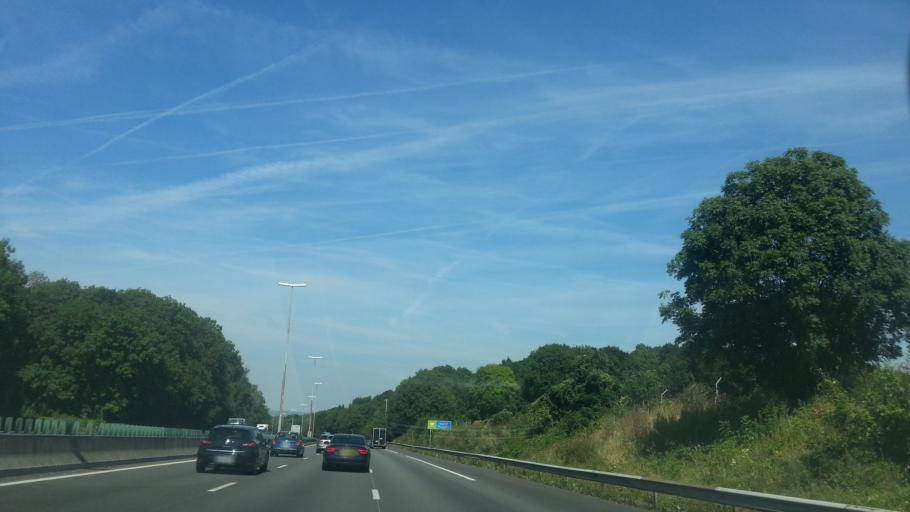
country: FR
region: Ile-de-France
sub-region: Departement du Val-d'Oise
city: Survilliers
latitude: 49.1155
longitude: 2.5549
